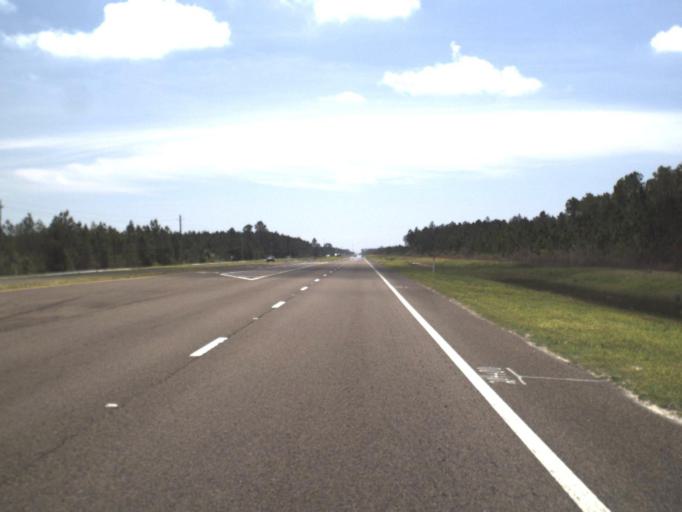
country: US
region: Florida
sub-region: Bay County
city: Laguna Beach
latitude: 30.2721
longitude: -85.8698
